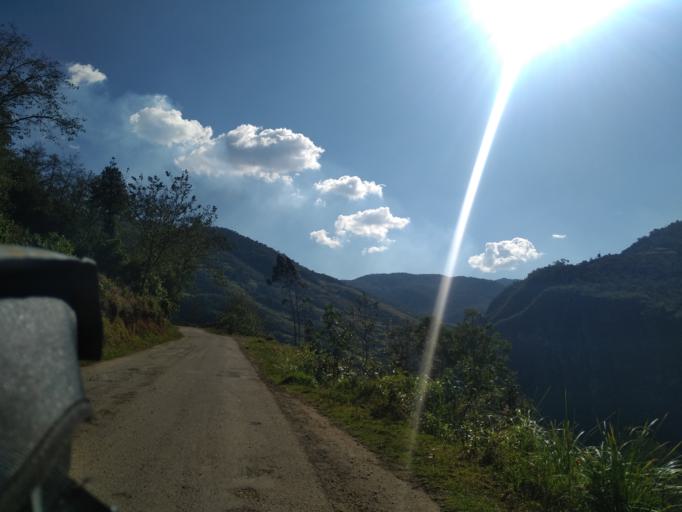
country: PE
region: Amazonas
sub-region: Provincia de Chachapoyas
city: Montevideo
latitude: -6.7147
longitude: -77.8183
